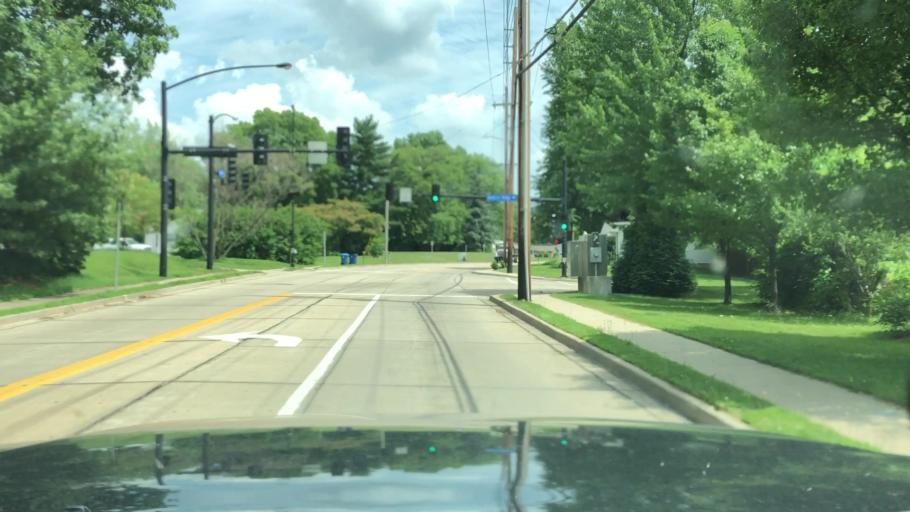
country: US
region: Missouri
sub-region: Saint Charles County
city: Saint Charles
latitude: 38.8066
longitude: -90.5095
